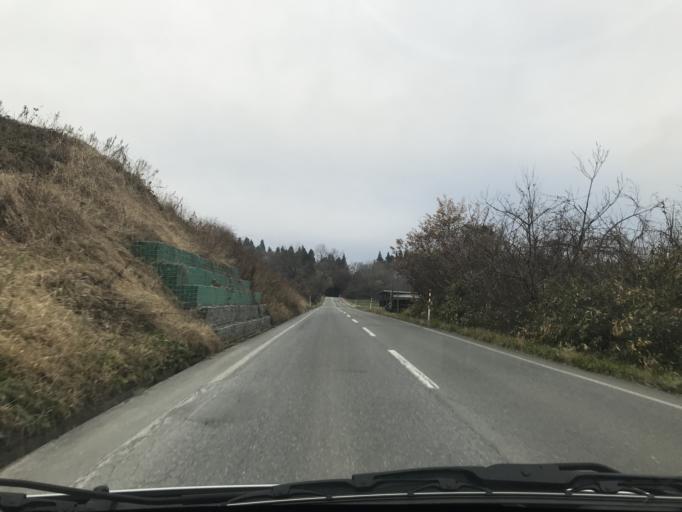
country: JP
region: Iwate
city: Kitakami
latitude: 39.2543
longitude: 141.2677
